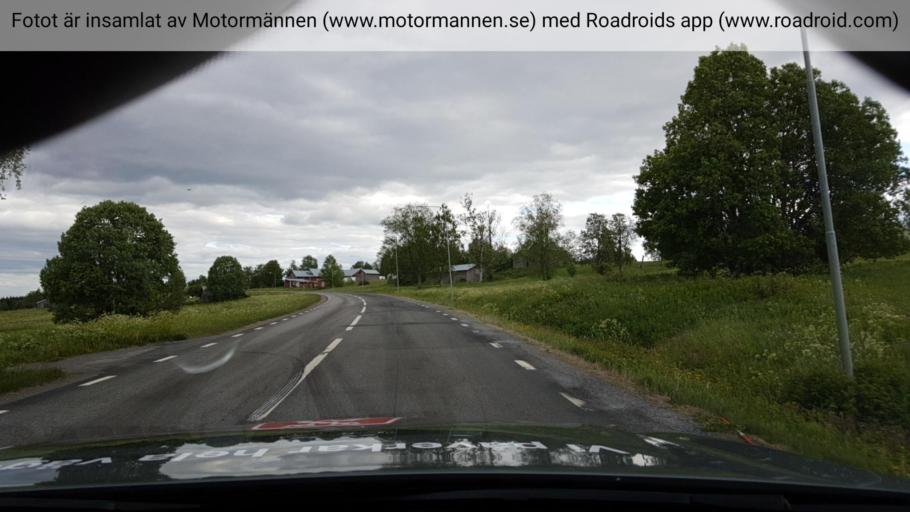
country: SE
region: Jaemtland
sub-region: Stroemsunds Kommun
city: Stroemsund
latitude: 63.8226
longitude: 15.5147
